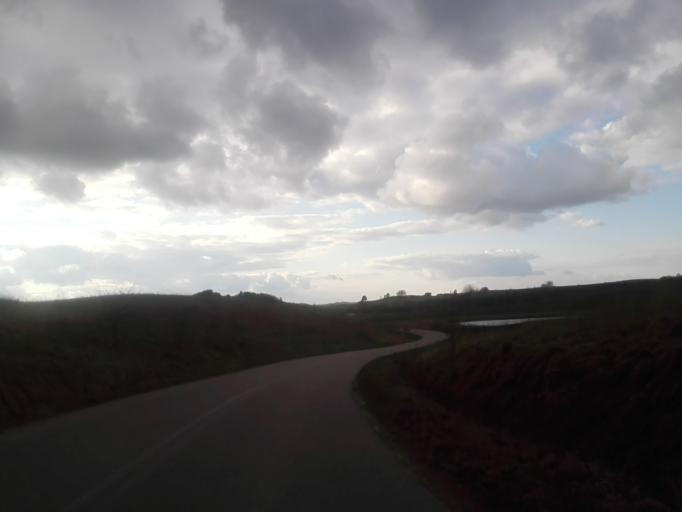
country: PL
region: Podlasie
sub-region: Suwalki
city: Suwalki
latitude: 54.1992
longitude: 22.9938
